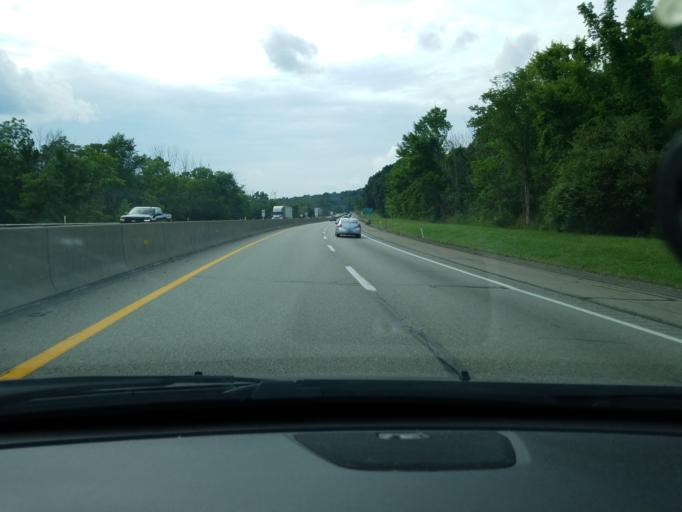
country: US
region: Pennsylvania
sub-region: Beaver County
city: Big Beaver
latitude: 40.8214
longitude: -80.3442
